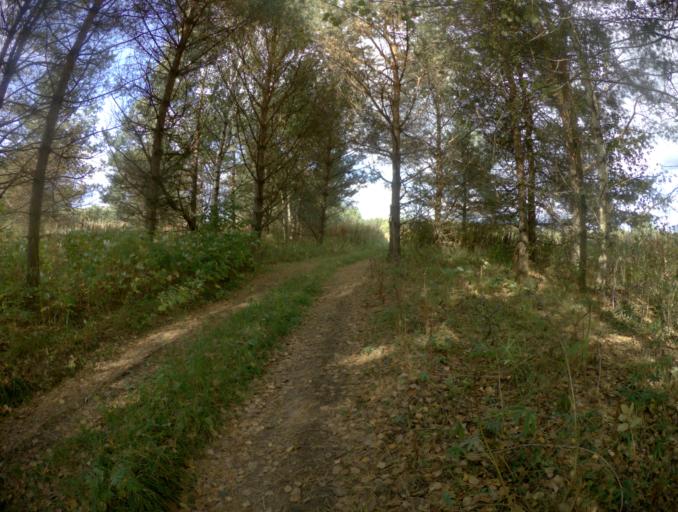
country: RU
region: Vladimir
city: Ivanishchi
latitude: 55.8505
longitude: 40.3971
